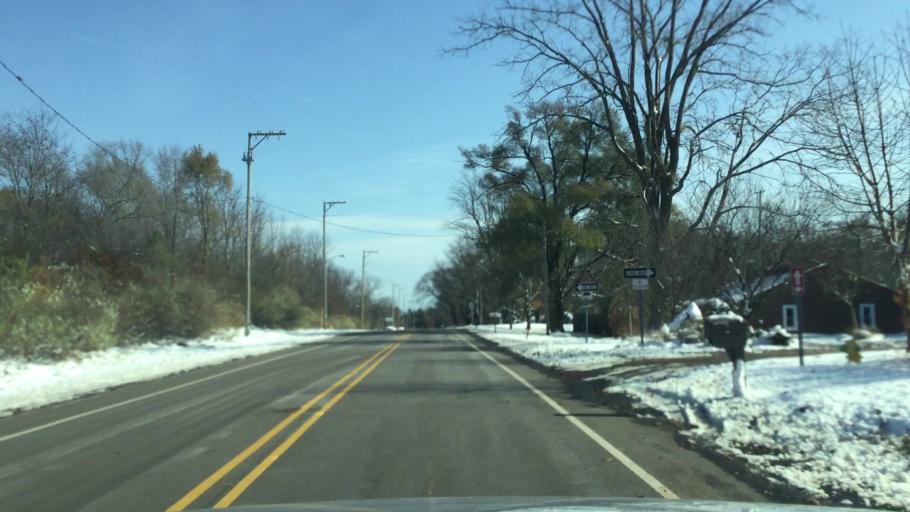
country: US
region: Michigan
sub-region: Kalamazoo County
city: Portage
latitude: 42.2211
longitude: -85.5662
